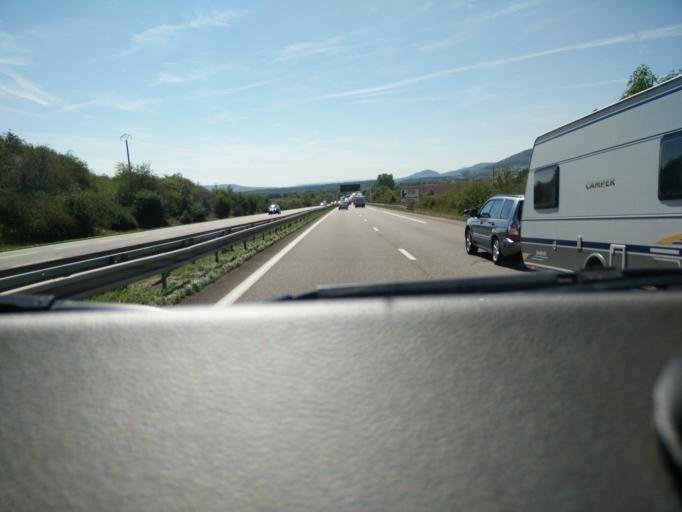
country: FR
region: Lorraine
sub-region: Departement de la Moselle
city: Entrange
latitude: 49.4530
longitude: 6.1206
